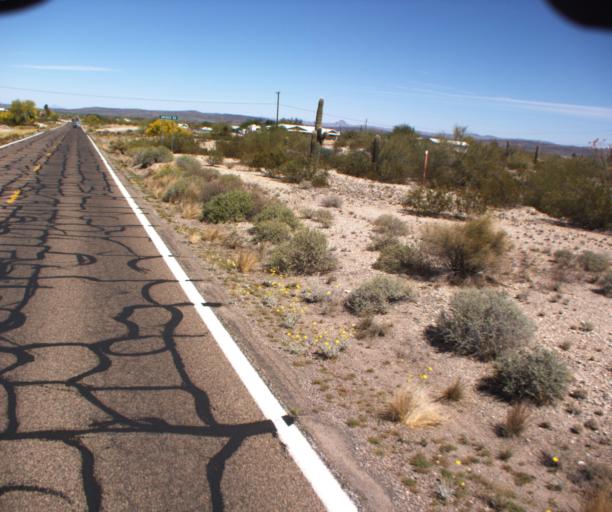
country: US
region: Arizona
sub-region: Pima County
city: Ajo
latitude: 32.3989
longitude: -112.8720
